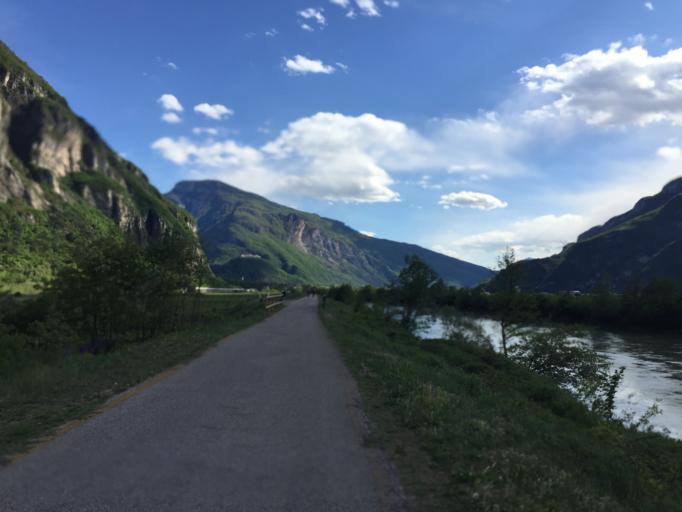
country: IT
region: Trentino-Alto Adige
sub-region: Provincia di Trento
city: Aldeno
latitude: 45.9697
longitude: 11.1088
